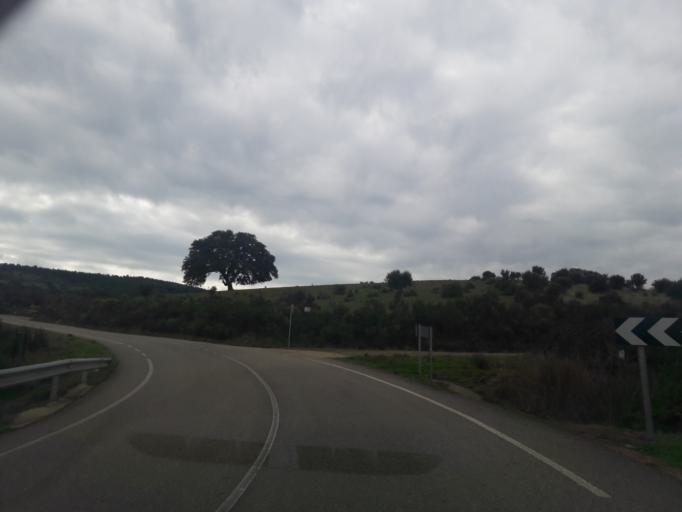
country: ES
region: Castille and Leon
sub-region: Provincia de Salamanca
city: Serradilla del Arroyo
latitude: 40.5232
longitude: -6.4032
